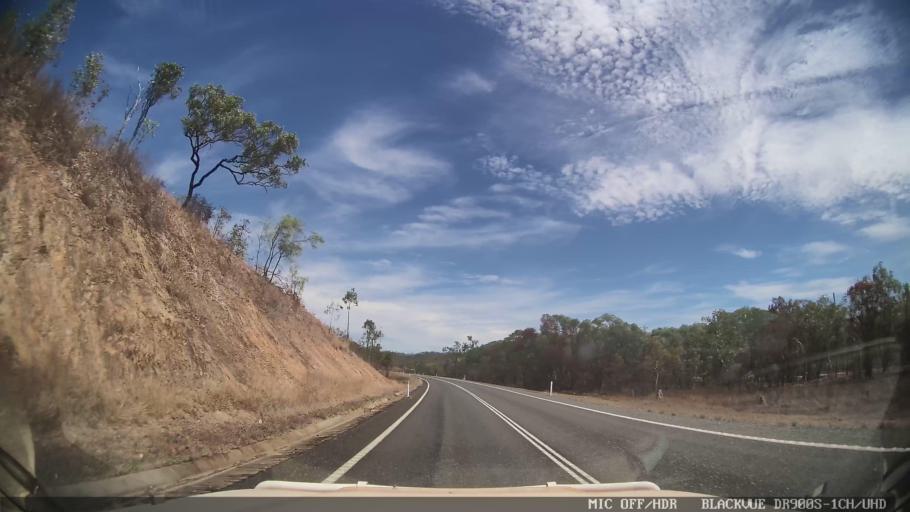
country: AU
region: Queensland
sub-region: Cook
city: Cooktown
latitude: -15.6970
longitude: 145.0312
